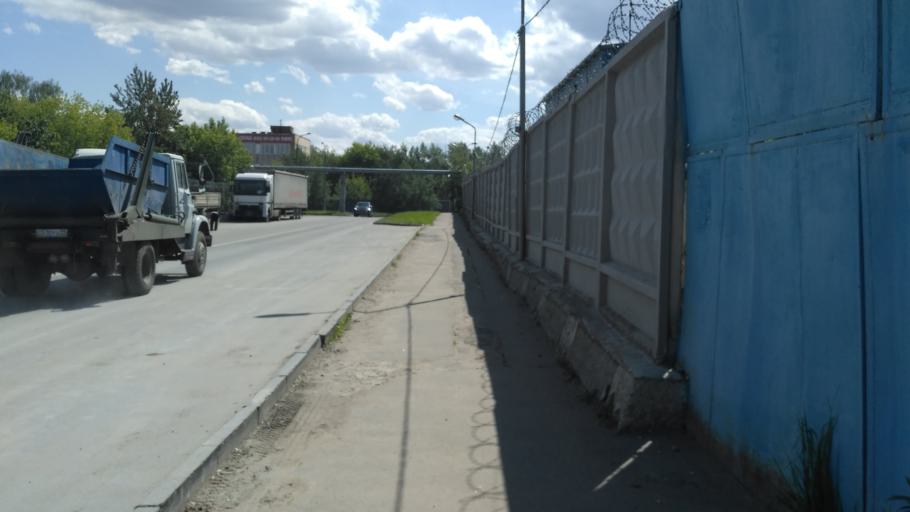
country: RU
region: Moscow
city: Kozeyevo
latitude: 55.8860
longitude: 37.6345
